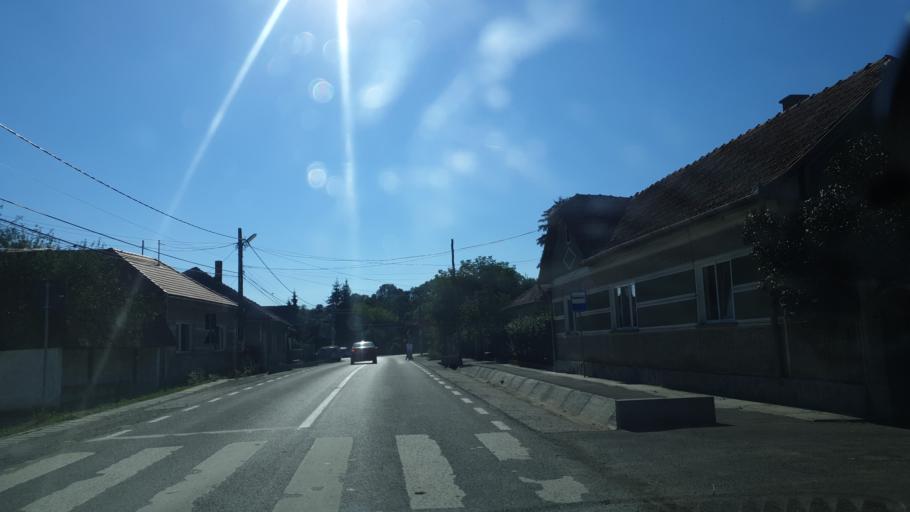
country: RO
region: Covasna
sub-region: Comuna Ilieni
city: Ilieni
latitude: 45.7939
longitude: 25.7696
